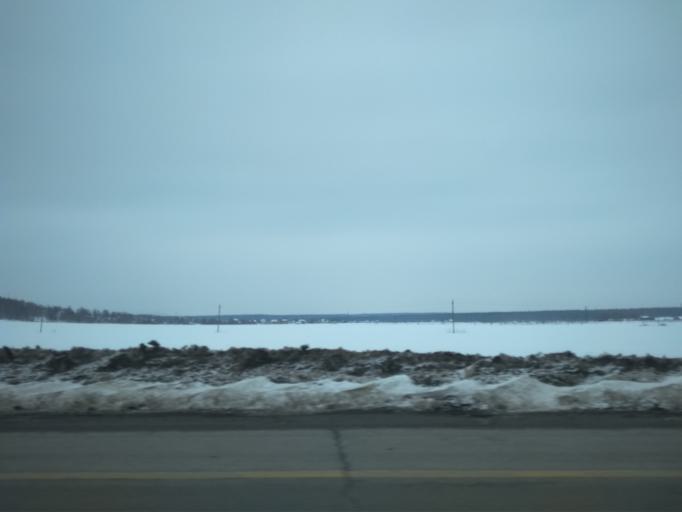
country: RU
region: Moskovskaya
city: Gorki-Leninskiye
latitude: 55.5004
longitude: 37.8401
